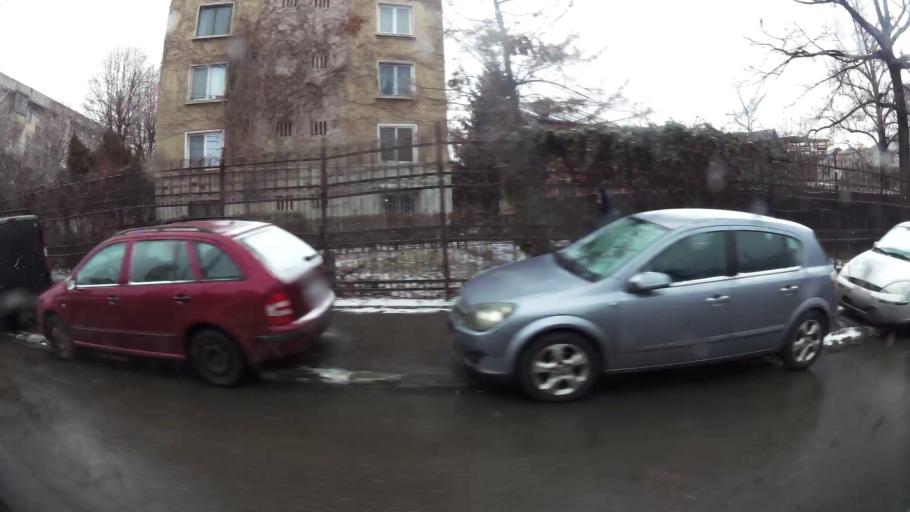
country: RO
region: Prahova
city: Ploiesti
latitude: 44.9391
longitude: 26.0141
